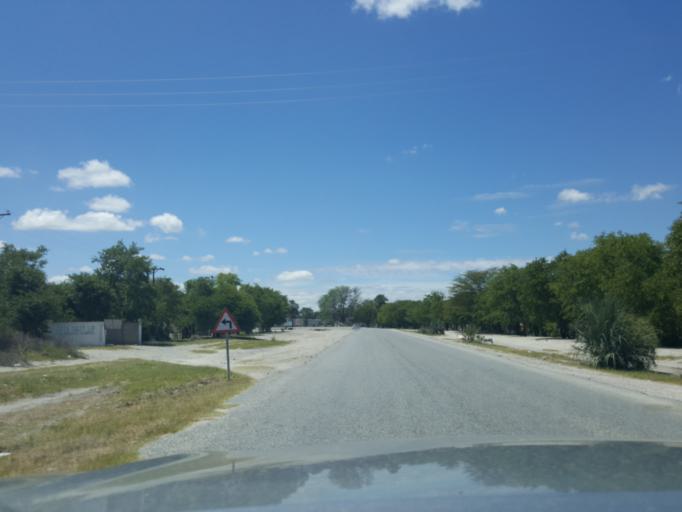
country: BW
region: Central
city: Nata
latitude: -20.2122
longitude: 26.1770
